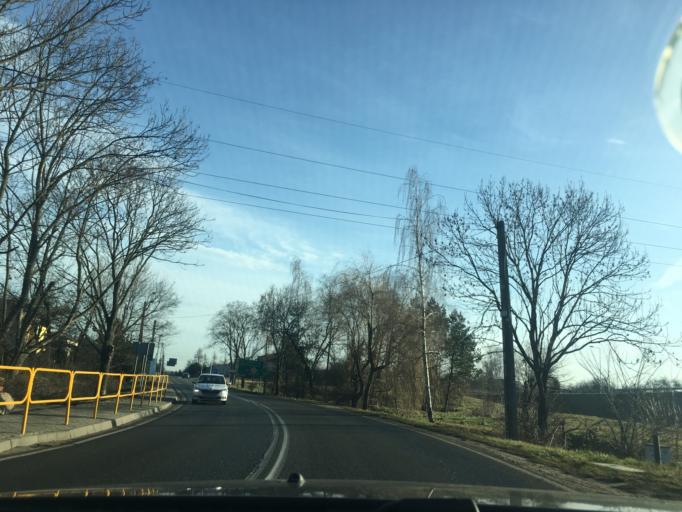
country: PL
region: Swietokrzyskie
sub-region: Powiat jedrzejowski
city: Jedrzejow
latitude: 50.6336
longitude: 20.3172
